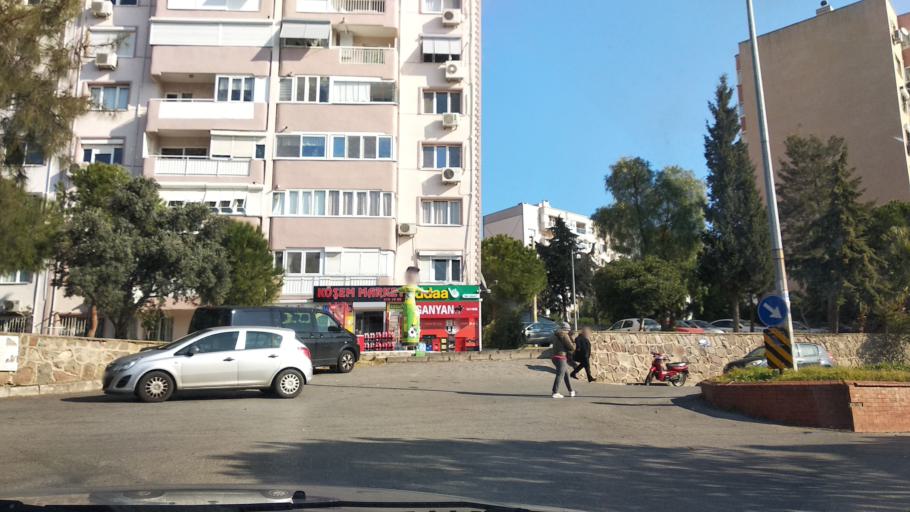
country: TR
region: Izmir
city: Karsiyaka
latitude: 38.4933
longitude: 27.0864
